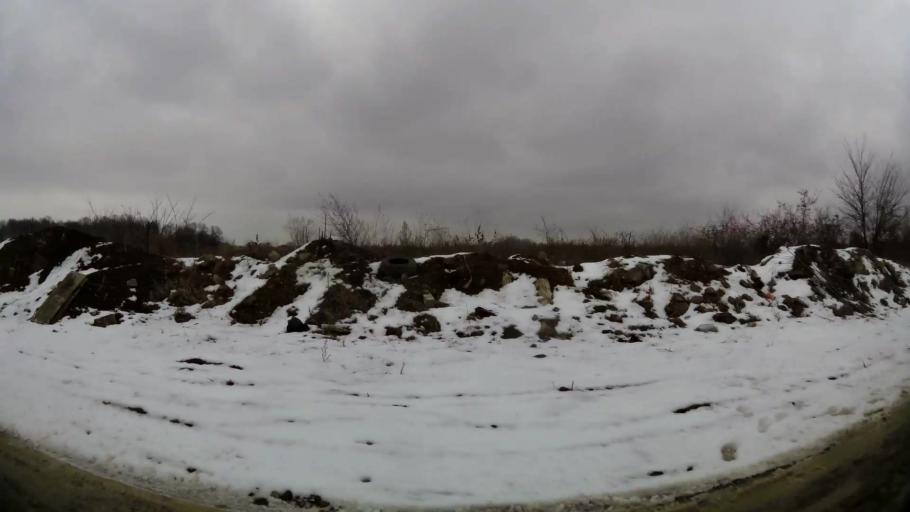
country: RO
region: Ilfov
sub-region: Comuna Mogosoaia
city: Mogosoaia
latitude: 44.5061
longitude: 26.0082
